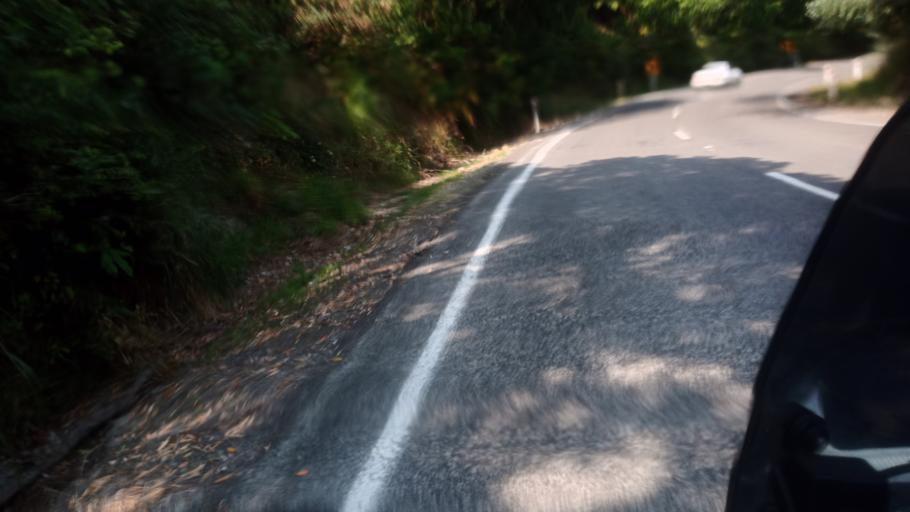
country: NZ
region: Bay of Plenty
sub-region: Opotiki District
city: Opotiki
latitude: -37.6092
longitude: 177.9607
